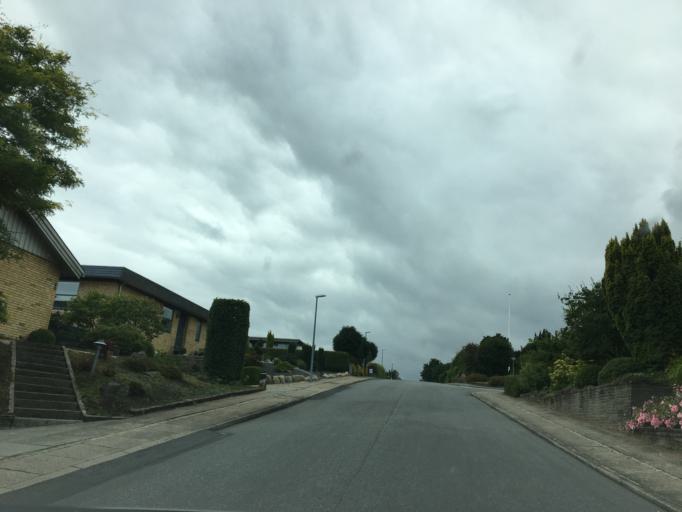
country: DK
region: South Denmark
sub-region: Vejle Kommune
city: Vejle
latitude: 55.7109
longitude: 9.5933
